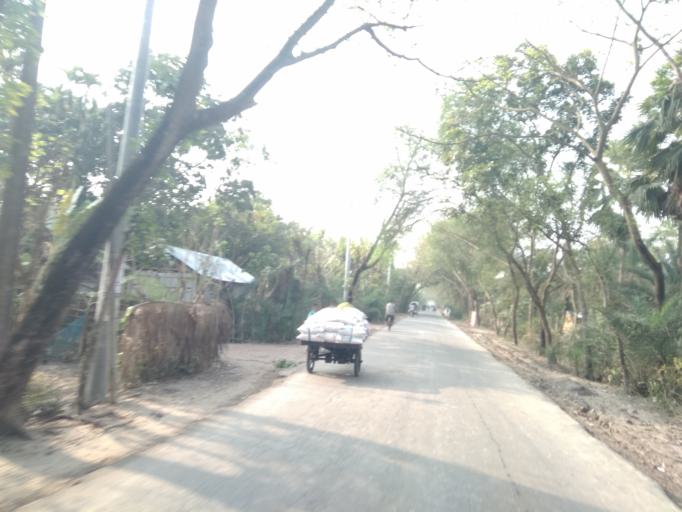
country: IN
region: West Bengal
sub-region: North 24 Parganas
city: Taki
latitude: 22.3246
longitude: 89.1056
